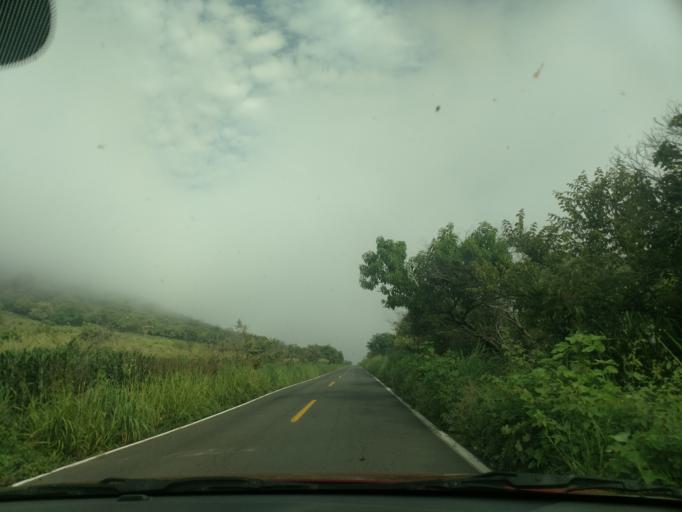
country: MX
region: Jalisco
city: Ameca
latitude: 20.5386
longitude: -104.1407
